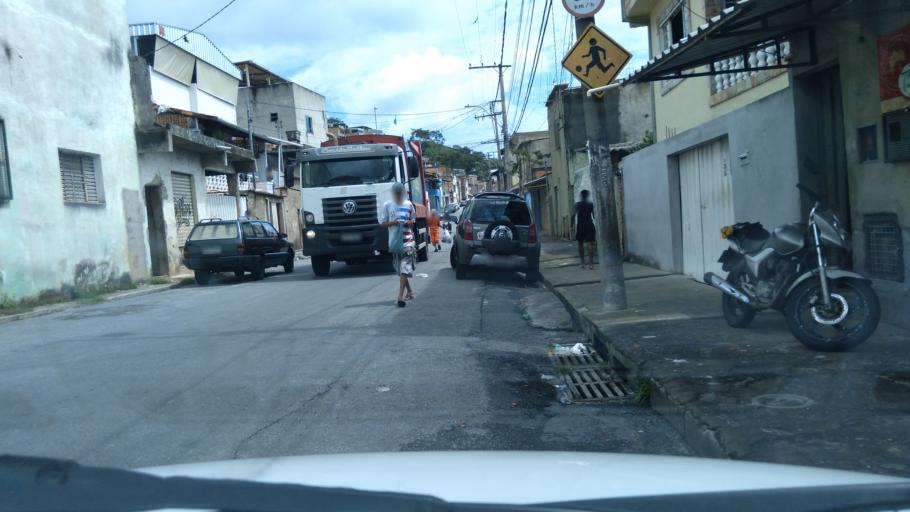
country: BR
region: Minas Gerais
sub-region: Belo Horizonte
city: Belo Horizonte
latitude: -19.8964
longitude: -43.8901
